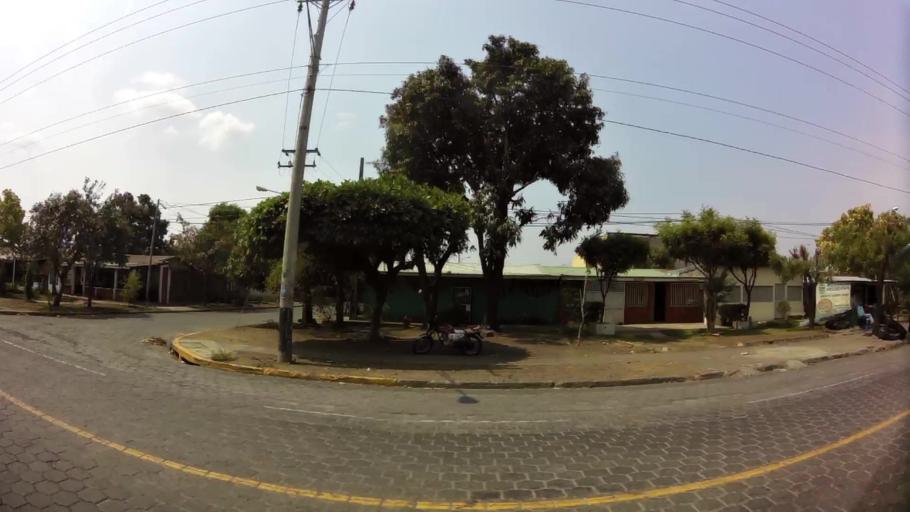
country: NI
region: Managua
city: Ciudad Sandino
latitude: 12.1582
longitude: -86.3035
